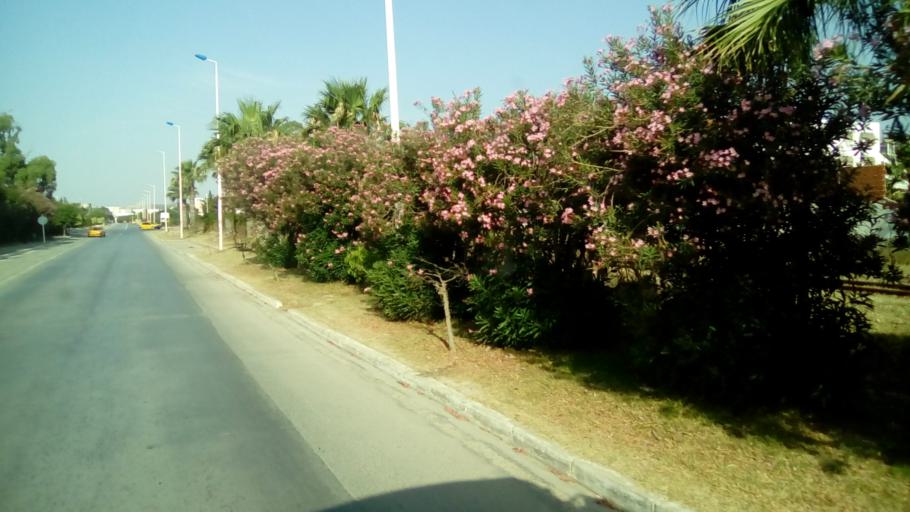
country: TN
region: Nabul
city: Nabeul
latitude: 36.4283
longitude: 10.6822
